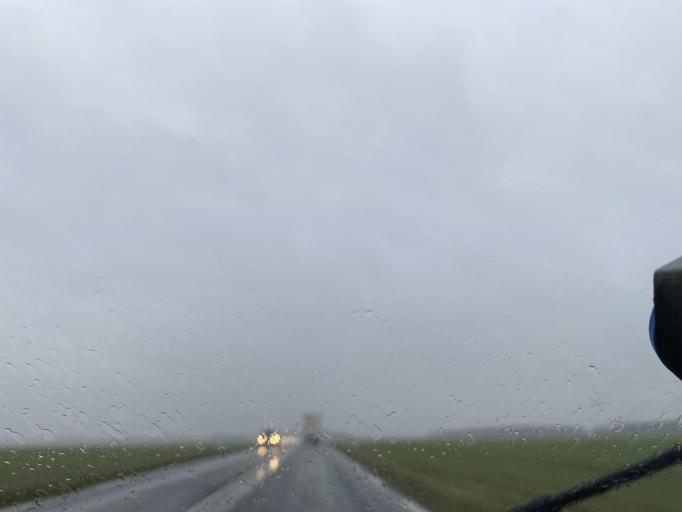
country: FR
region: Centre
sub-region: Departement d'Eure-et-Loir
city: Vernouillet
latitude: 48.7008
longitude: 1.3744
